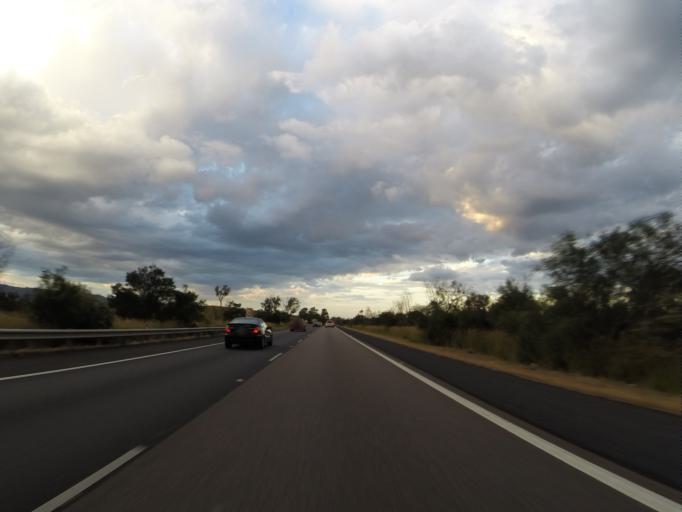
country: AU
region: New South Wales
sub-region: Wollondilly
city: Douglas Park
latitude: -34.2219
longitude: 150.6749
